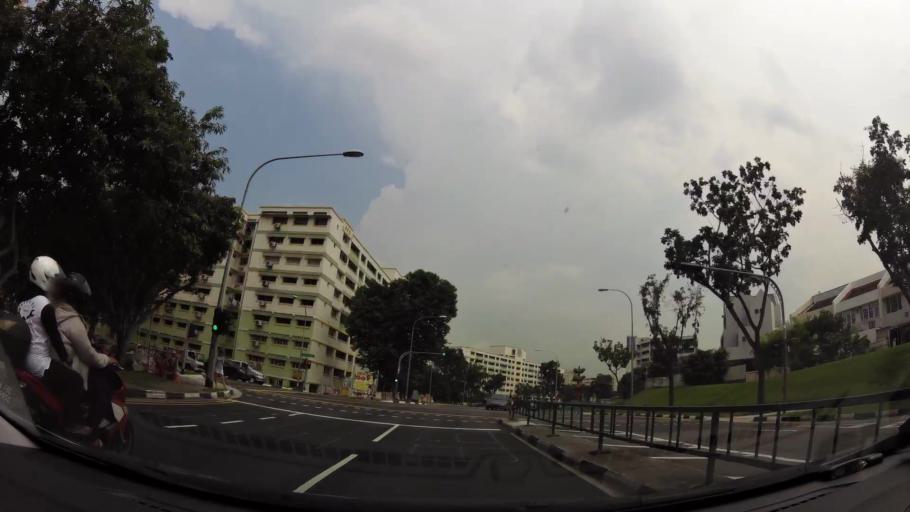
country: SG
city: Singapore
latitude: 1.3313
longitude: 103.9069
